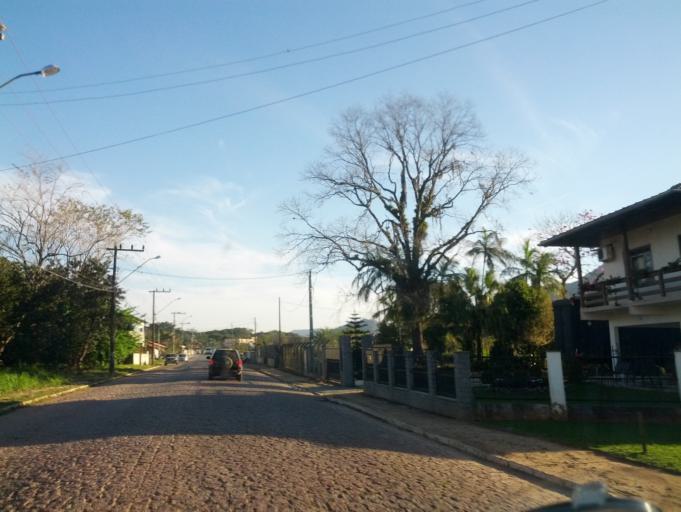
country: BR
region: Santa Catarina
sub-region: Indaial
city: Indaial
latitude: -26.9014
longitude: -49.2578
